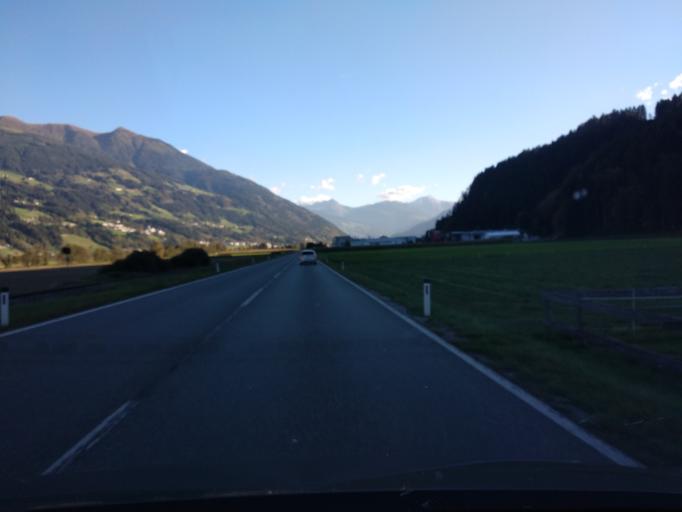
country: AT
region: Tyrol
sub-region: Politischer Bezirk Schwaz
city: Schlitters
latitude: 47.3720
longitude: 11.8466
